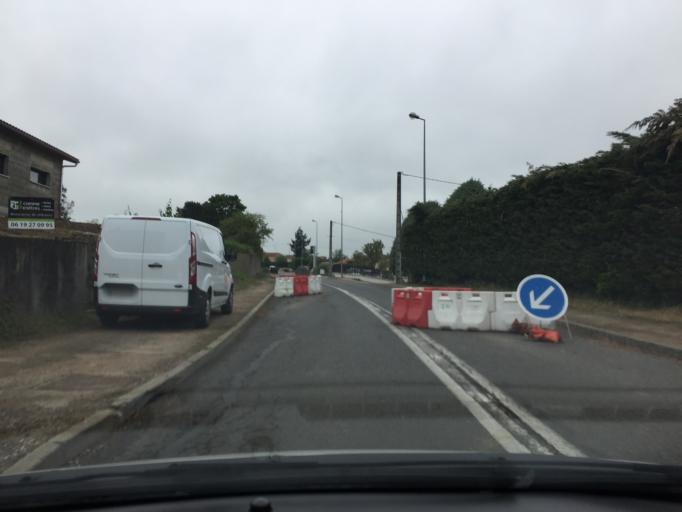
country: FR
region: Rhone-Alpes
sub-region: Departement du Rhone
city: Mornant
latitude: 45.6190
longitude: 4.6843
